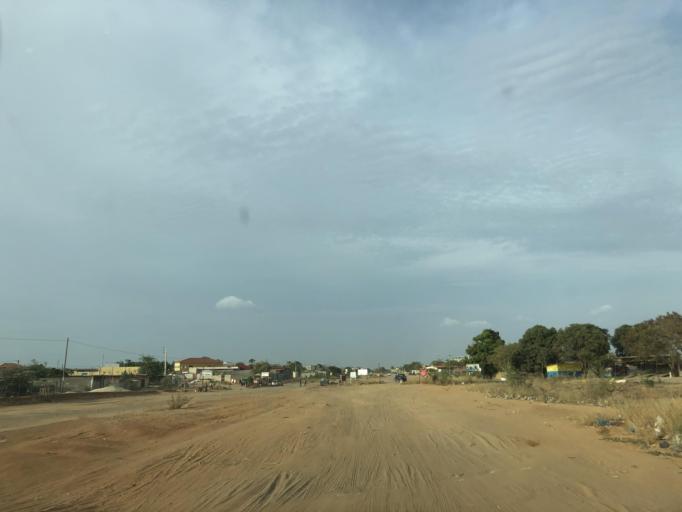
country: AO
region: Luanda
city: Luanda
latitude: -8.9201
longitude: 13.3089
